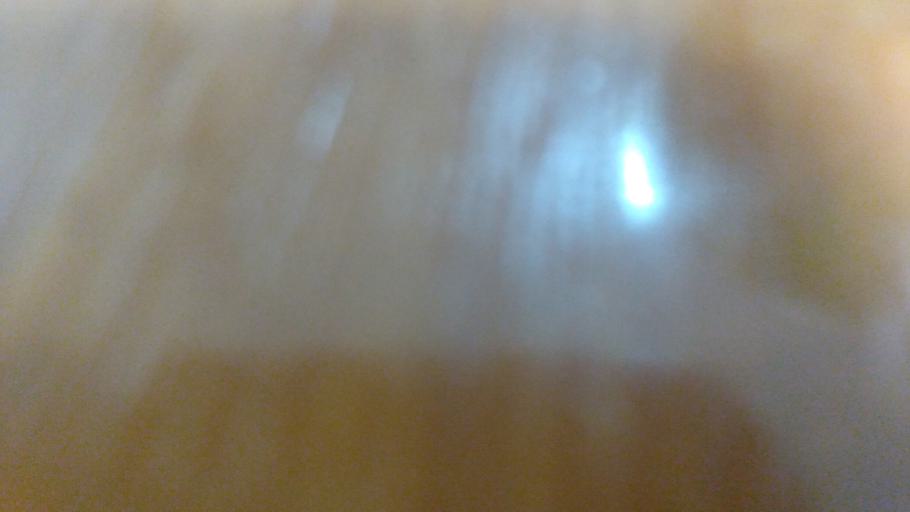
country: RU
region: Republic of Karelia
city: Shal'skiy
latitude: 61.9582
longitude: 36.1729
